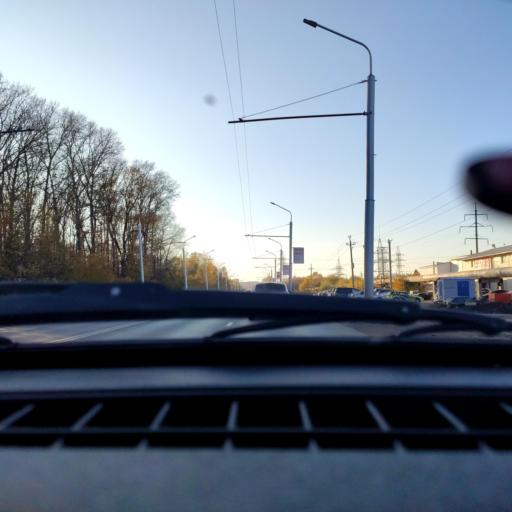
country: RU
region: Bashkortostan
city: Ufa
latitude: 54.7920
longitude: 56.0953
